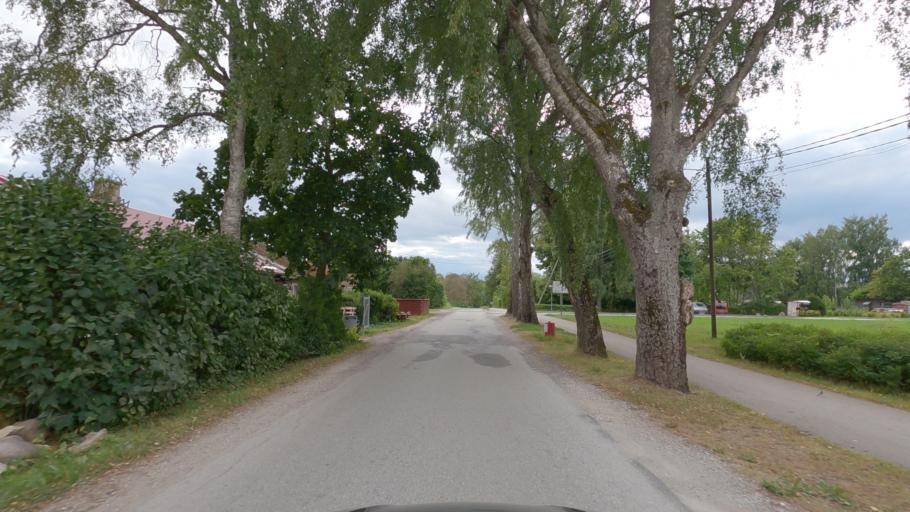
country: EE
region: Raplamaa
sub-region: Kohila vald
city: Kohila
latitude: 59.1752
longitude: 24.7565
